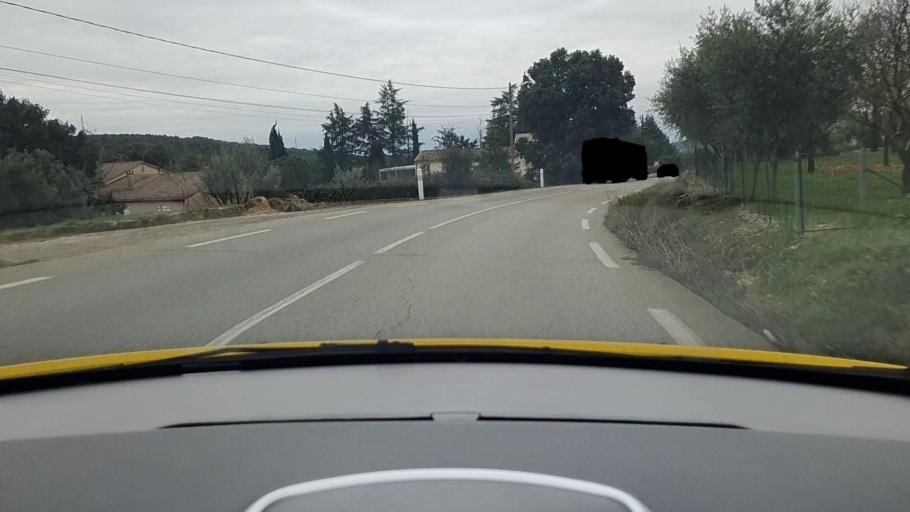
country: FR
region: Languedoc-Roussillon
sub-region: Departement du Gard
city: Laval-Pradel
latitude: 44.1910
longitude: 4.0850
